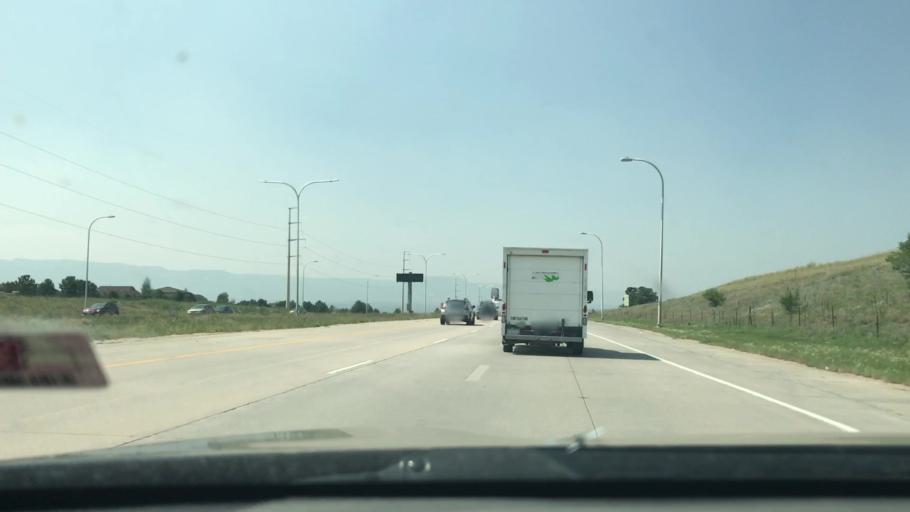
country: US
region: Colorado
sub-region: El Paso County
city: Black Forest
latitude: 38.9775
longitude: -104.7547
